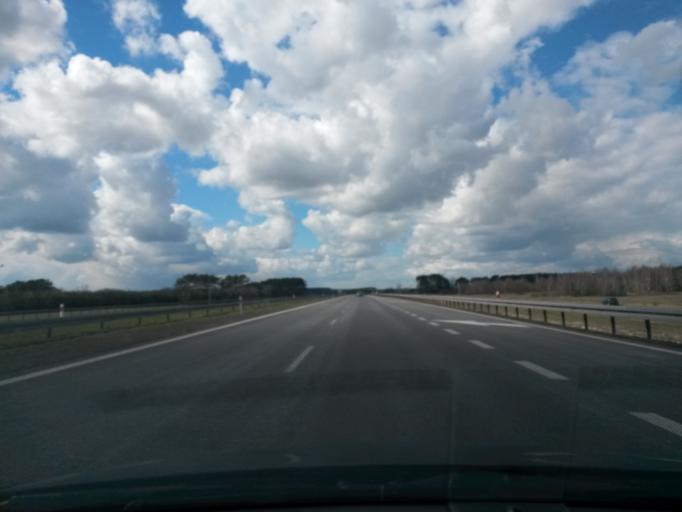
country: PL
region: Greater Poland Voivodeship
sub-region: Powiat kolski
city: Dabie
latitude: 52.0987
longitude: 18.7690
